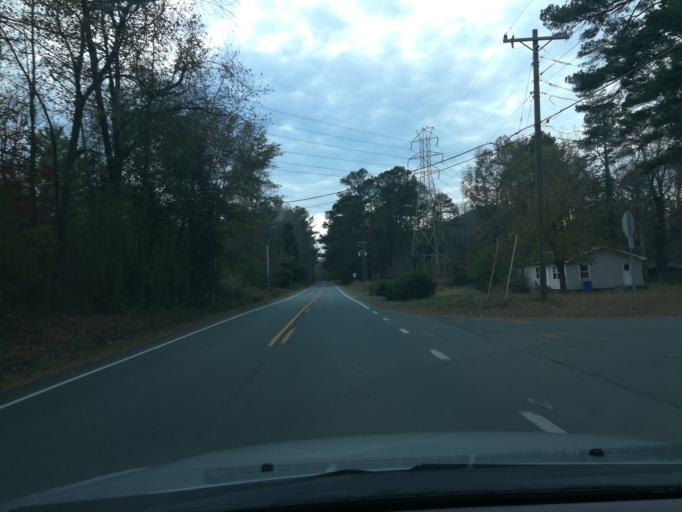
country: US
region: North Carolina
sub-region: Orange County
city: Hillsborough
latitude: 36.0307
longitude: -79.0020
